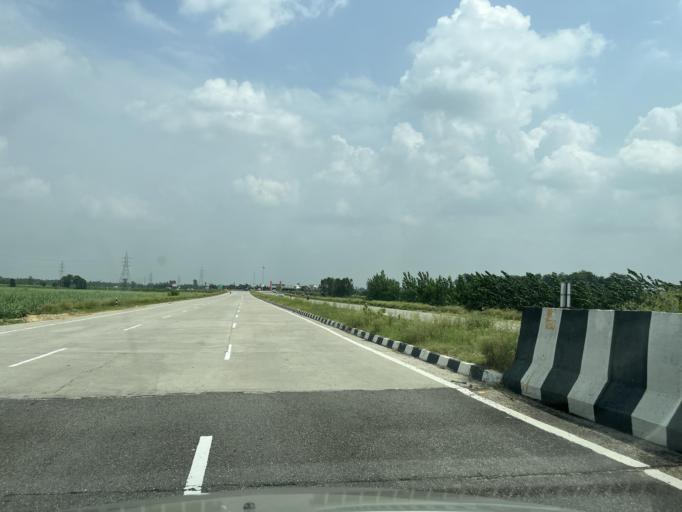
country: IN
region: Uttar Pradesh
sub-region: Bijnor
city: Dhampur
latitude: 29.3178
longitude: 78.5335
